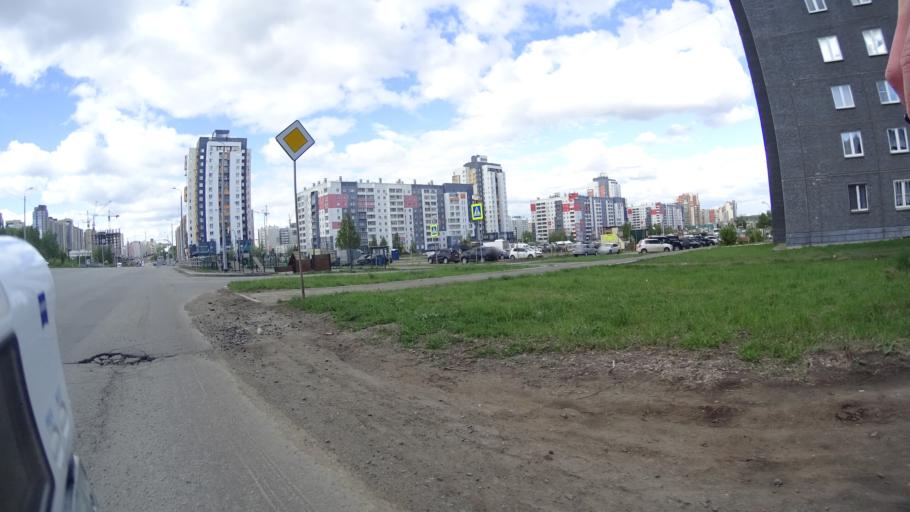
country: RU
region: Chelyabinsk
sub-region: Gorod Chelyabinsk
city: Chelyabinsk
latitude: 55.1625
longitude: 61.2860
